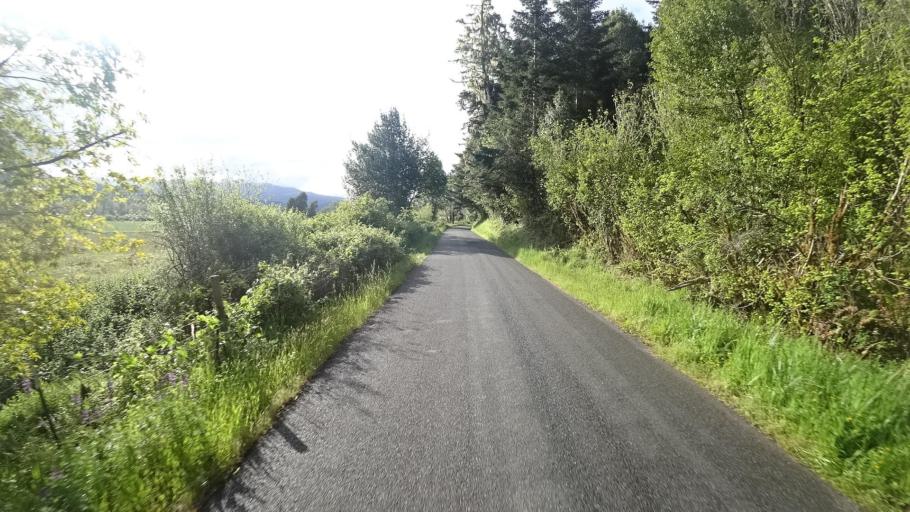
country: US
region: California
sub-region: Humboldt County
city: Blue Lake
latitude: 40.8801
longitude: -124.0159
